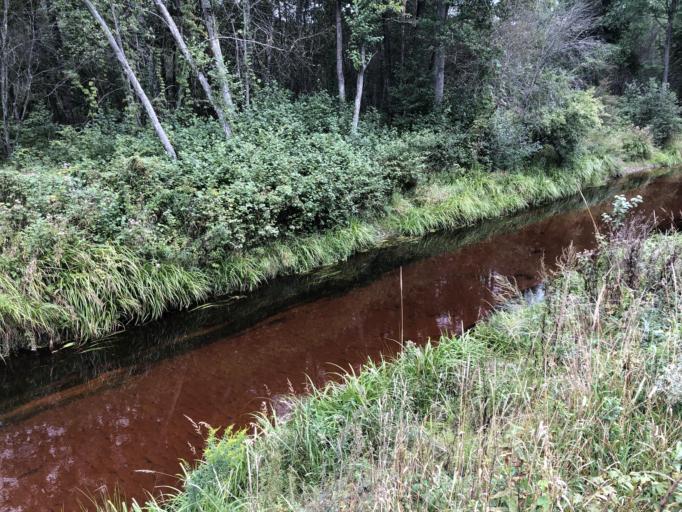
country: LV
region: Vecumnieki
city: Vecumnieki
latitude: 56.6482
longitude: 24.4708
